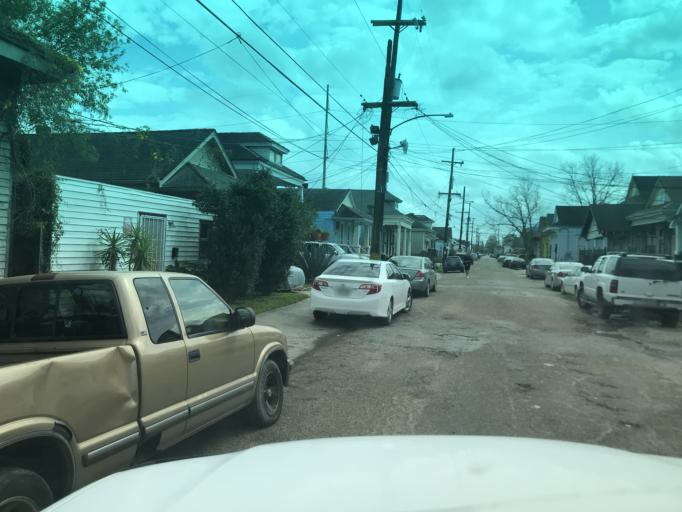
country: US
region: Louisiana
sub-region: Orleans Parish
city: New Orleans
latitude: 29.9767
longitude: -90.0562
